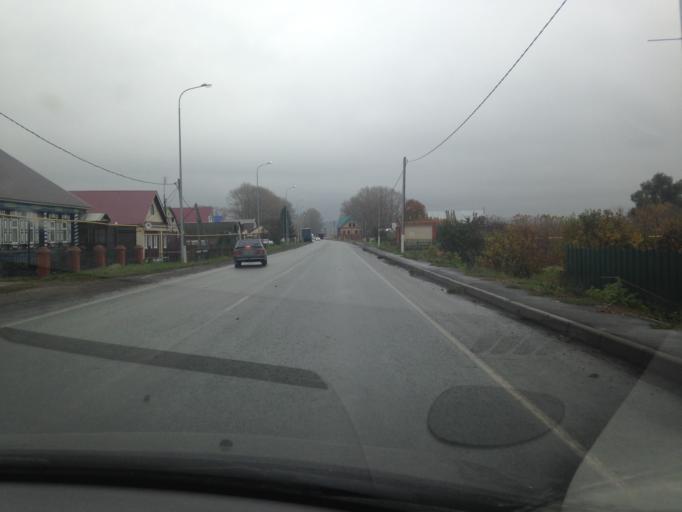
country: RU
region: Tatarstan
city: Buinsk
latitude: 54.9963
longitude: 48.3362
